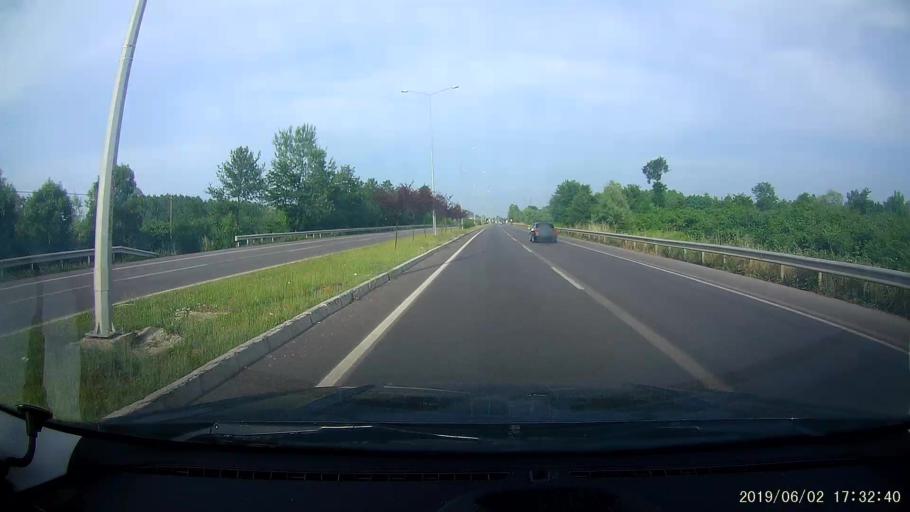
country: TR
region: Samsun
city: Carsamba
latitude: 41.2204
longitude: 36.8317
